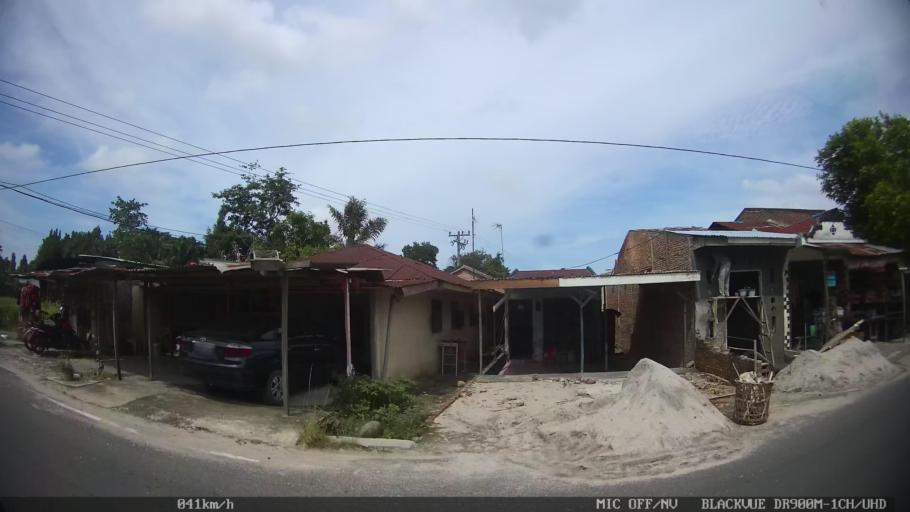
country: ID
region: North Sumatra
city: Percut
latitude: 3.6009
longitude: 98.8585
